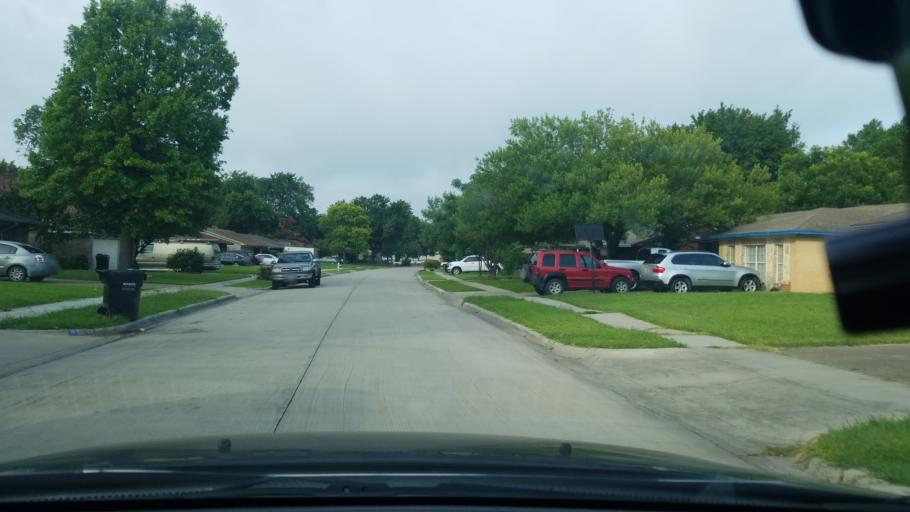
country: US
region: Texas
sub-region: Dallas County
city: Garland
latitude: 32.8315
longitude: -96.6514
